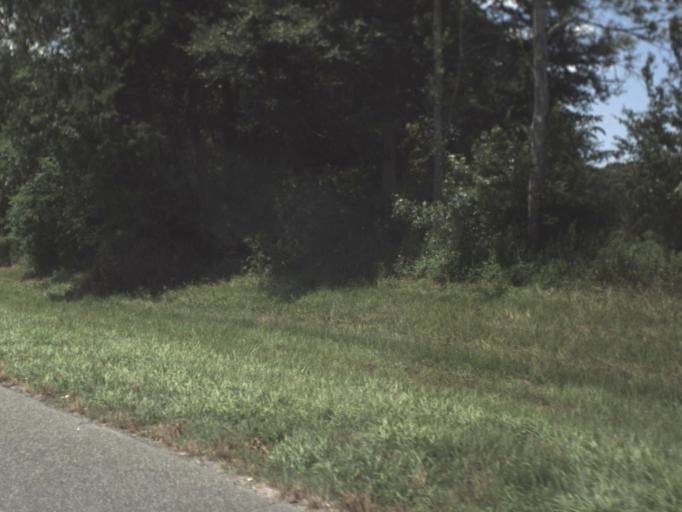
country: US
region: Florida
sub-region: Lafayette County
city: Mayo
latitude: 29.9880
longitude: -83.0041
